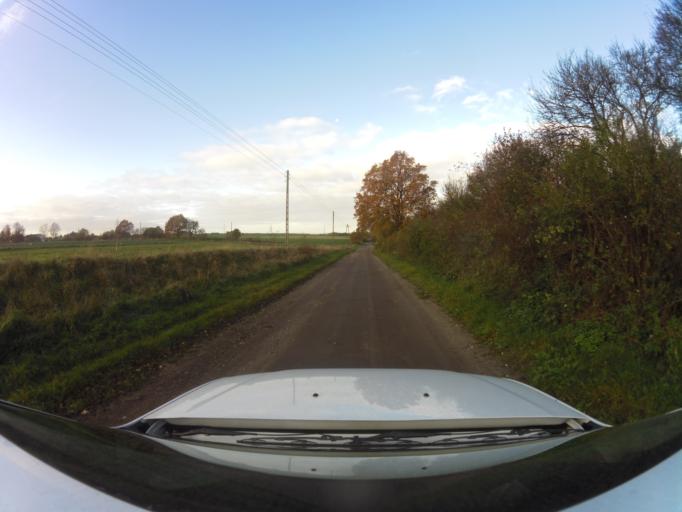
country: PL
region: West Pomeranian Voivodeship
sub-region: Powiat gryficki
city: Trzebiatow
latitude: 54.0492
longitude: 15.2030
